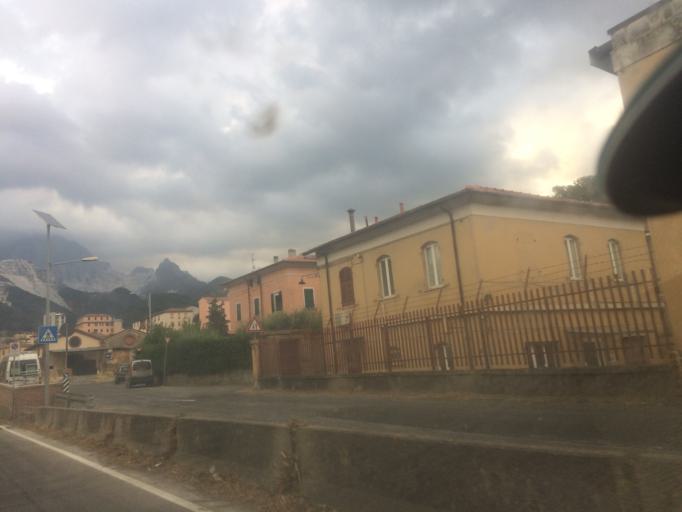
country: IT
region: Tuscany
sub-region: Provincia di Massa-Carrara
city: Carrara
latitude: 44.0736
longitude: 10.0914
